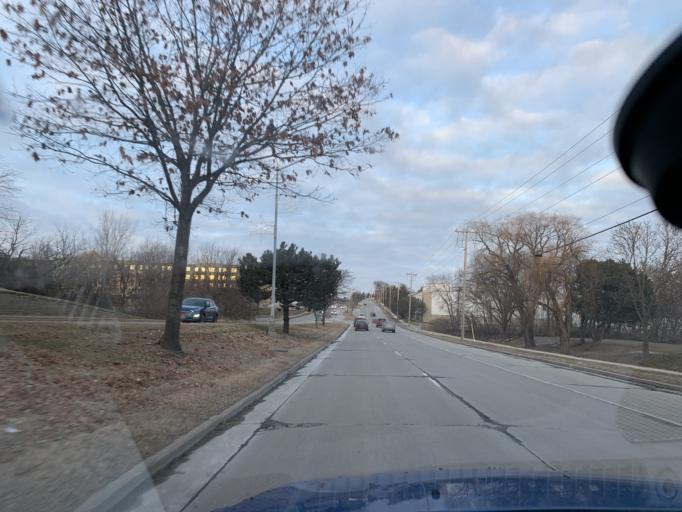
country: US
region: Wisconsin
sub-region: Dane County
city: Madison
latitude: 43.0220
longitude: -89.4166
